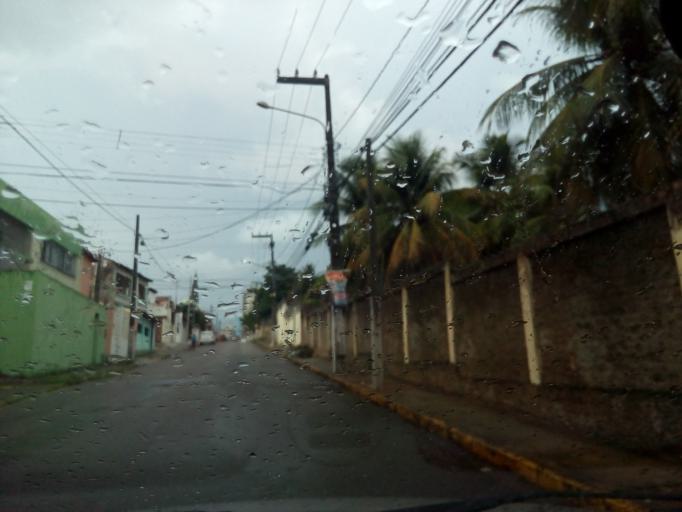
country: BR
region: Rio Grande do Norte
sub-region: Natal
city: Natal
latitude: -5.7924
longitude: -35.2067
